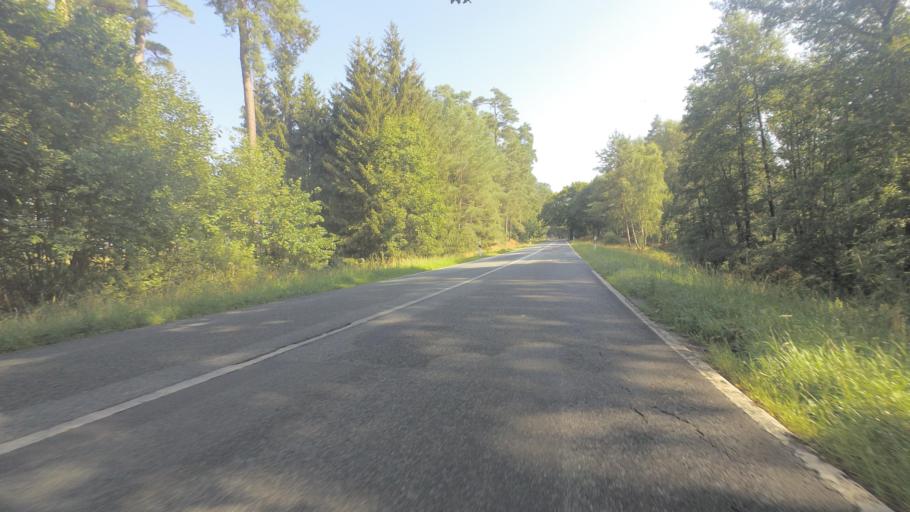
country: DE
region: Mecklenburg-Vorpommern
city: Malchow
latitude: 53.5741
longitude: 12.4581
